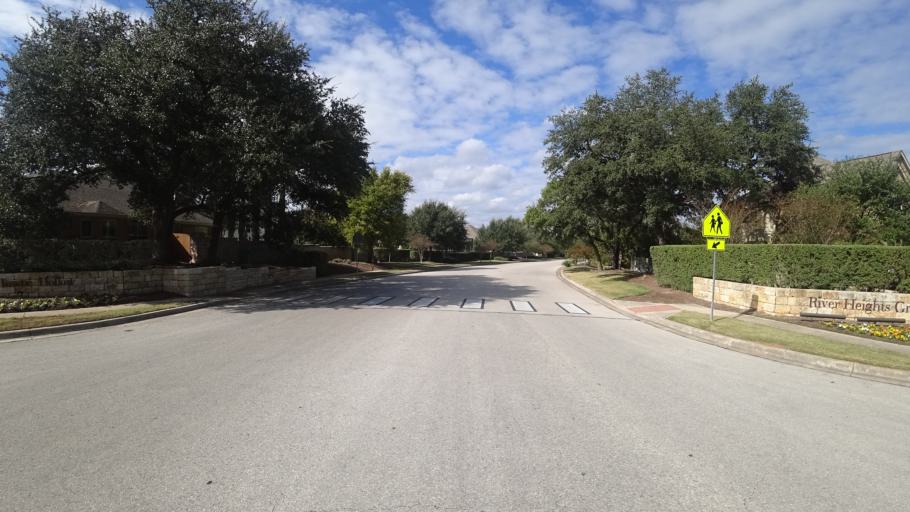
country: US
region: Texas
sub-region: Travis County
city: Hudson Bend
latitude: 30.3670
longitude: -97.9051
